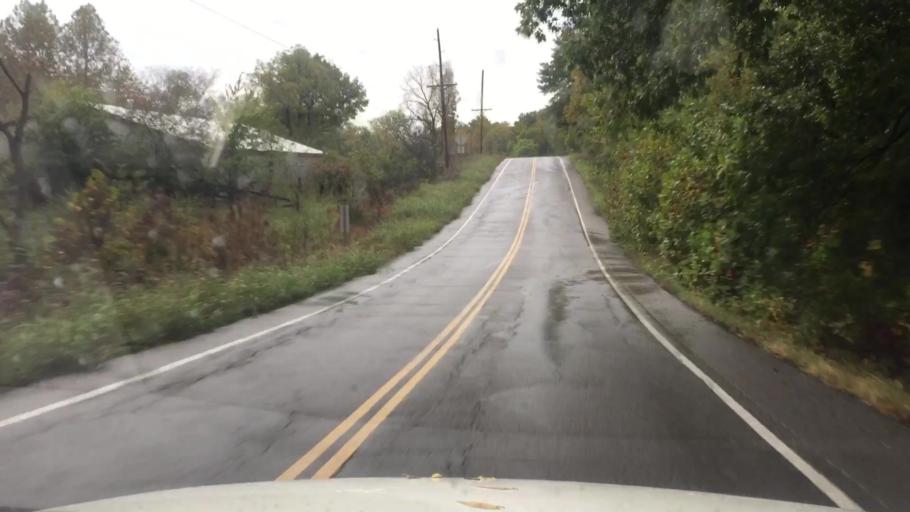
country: US
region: Missouri
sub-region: Boone County
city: Columbia
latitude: 38.8837
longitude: -92.4256
